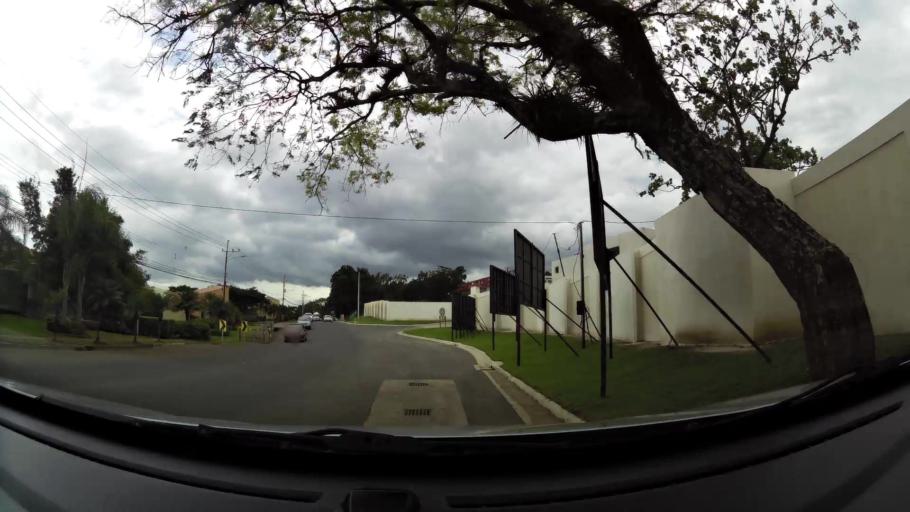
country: CR
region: Heredia
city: La Asuncion
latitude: 9.9584
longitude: -84.1709
